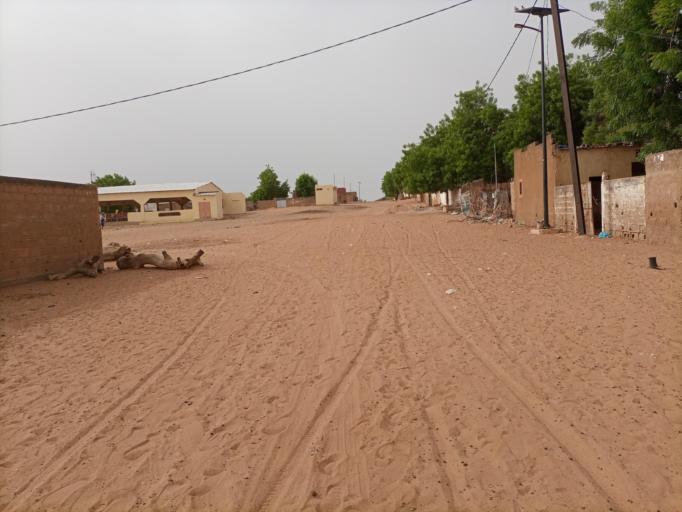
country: SN
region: Louga
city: Ndibene Dahra
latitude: 15.4014
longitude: -15.1174
